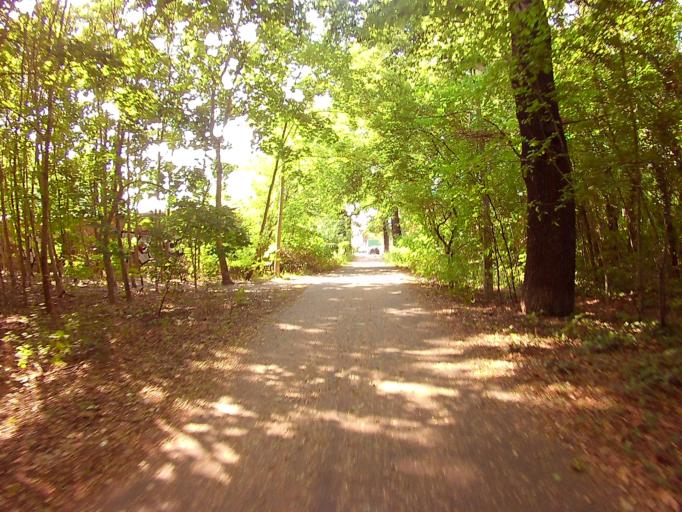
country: DE
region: Berlin
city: Oberschoneweide
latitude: 52.4767
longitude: 13.5133
